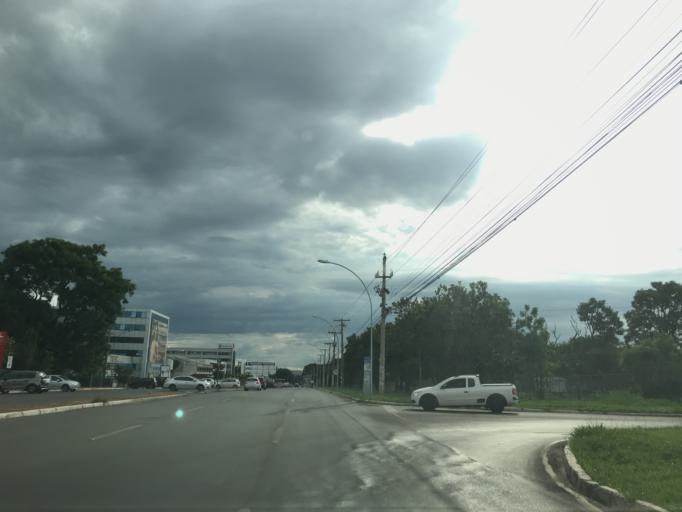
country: BR
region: Federal District
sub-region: Brasilia
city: Brasilia
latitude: -15.8074
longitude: -47.9063
